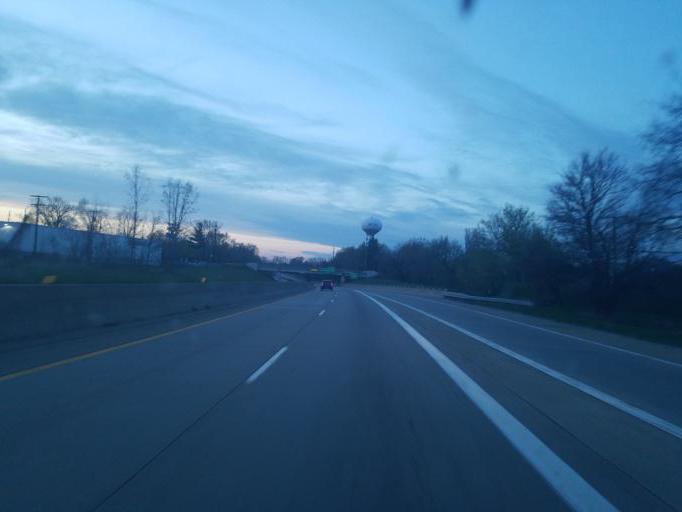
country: US
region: Michigan
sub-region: Washtenaw County
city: Milan
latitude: 42.0826
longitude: -83.6711
